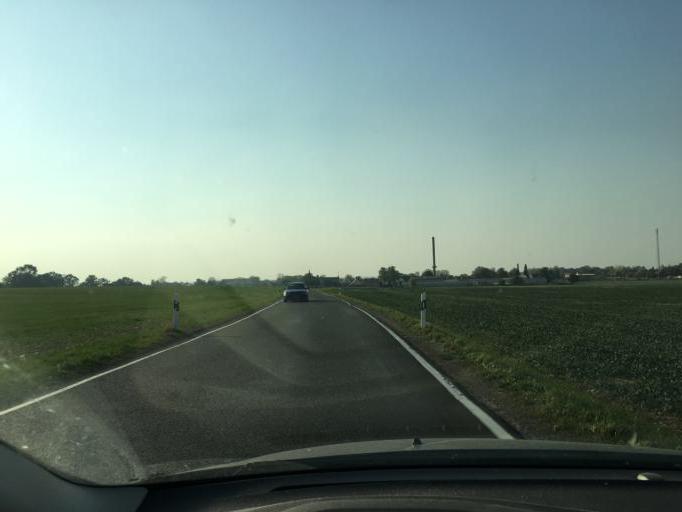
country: DE
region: Saxony
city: Nerchau
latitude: 51.3291
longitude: 12.8183
